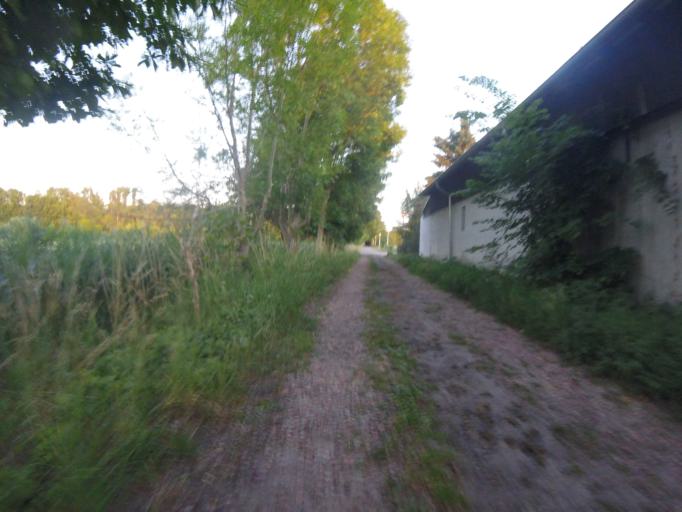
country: DE
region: Brandenburg
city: Konigs Wusterhausen
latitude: 52.2835
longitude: 13.5928
